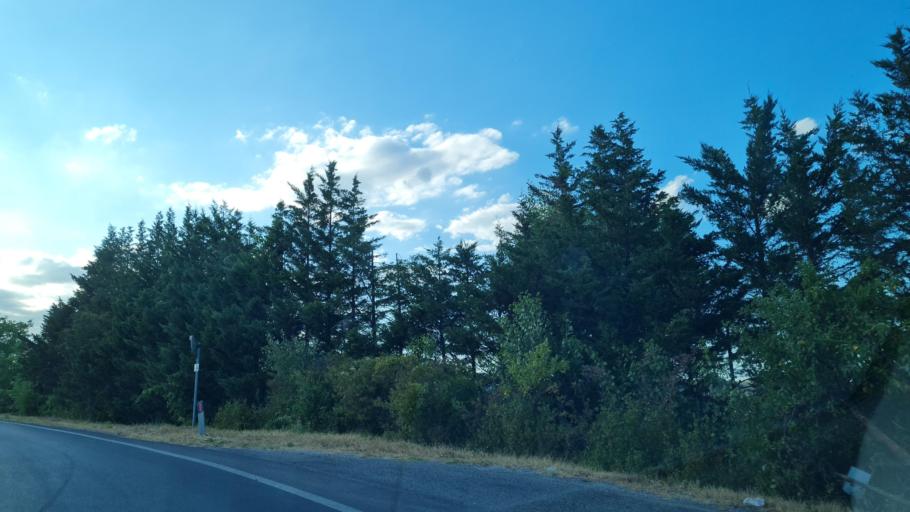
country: IT
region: Tuscany
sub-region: Provincia di Siena
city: Chianciano Terme
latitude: 43.0370
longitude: 11.8307
